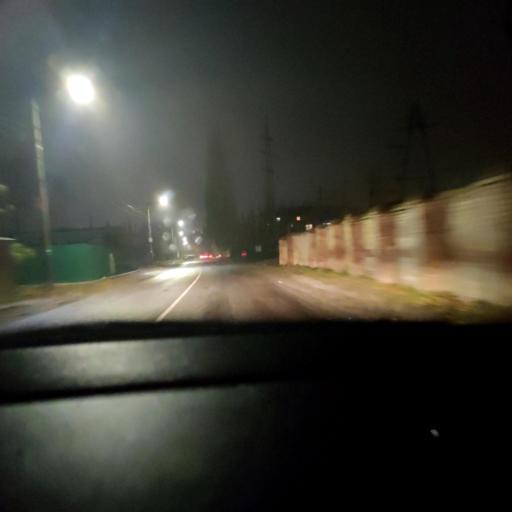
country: RU
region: Voronezj
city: Semiluki
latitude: 51.6860
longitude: 39.0210
